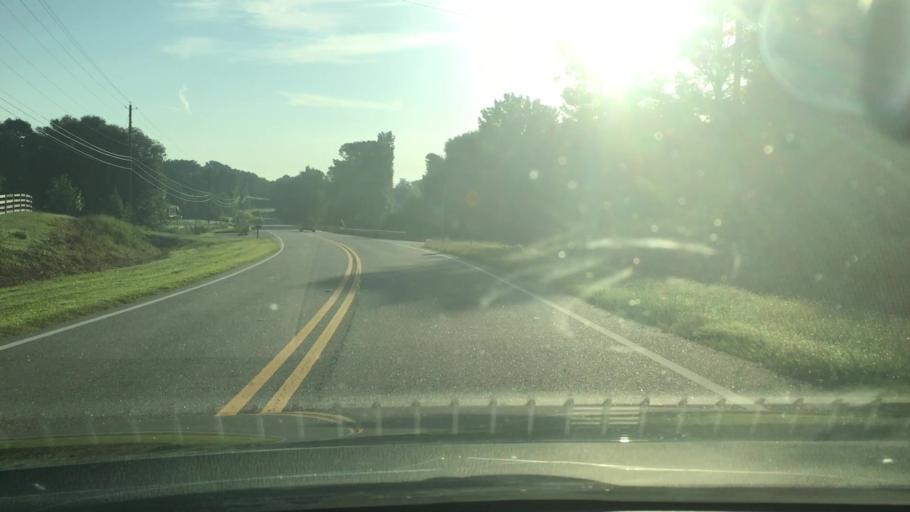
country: US
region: Georgia
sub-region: Fayette County
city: Peachtree City
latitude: 33.3935
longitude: -84.6315
